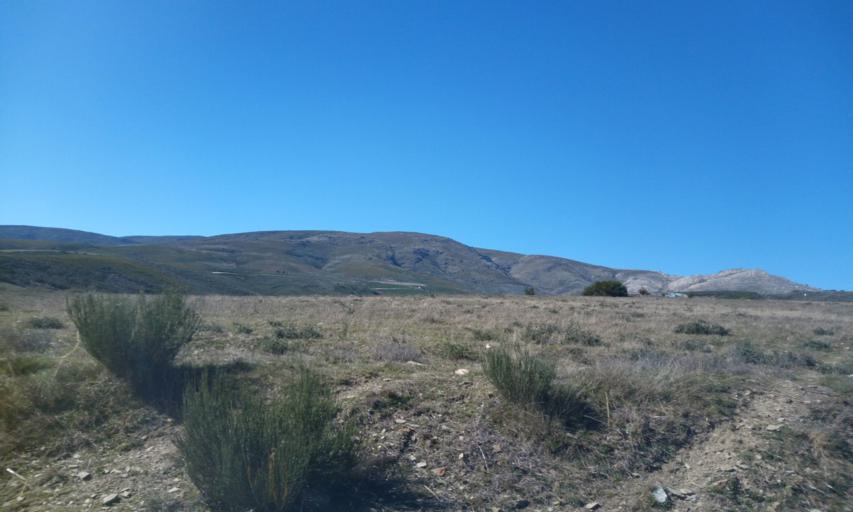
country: PT
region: Guarda
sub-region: Manteigas
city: Manteigas
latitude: 40.4576
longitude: -7.4938
